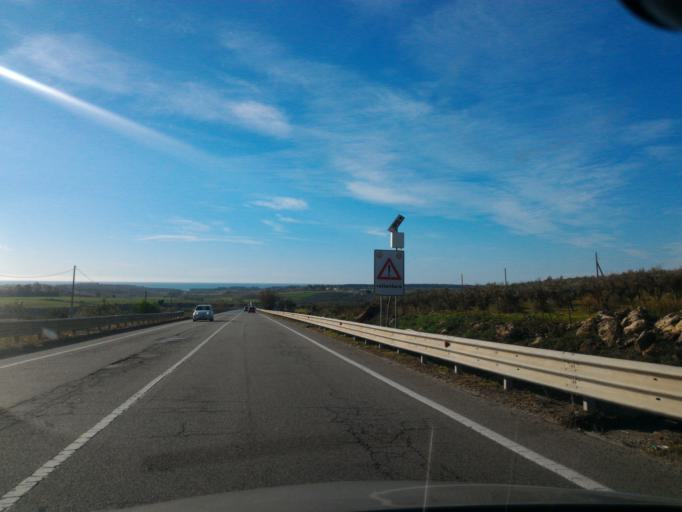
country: IT
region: Calabria
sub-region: Provincia di Crotone
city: Isola di Capo Rizzuto
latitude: 38.9460
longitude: 17.0819
